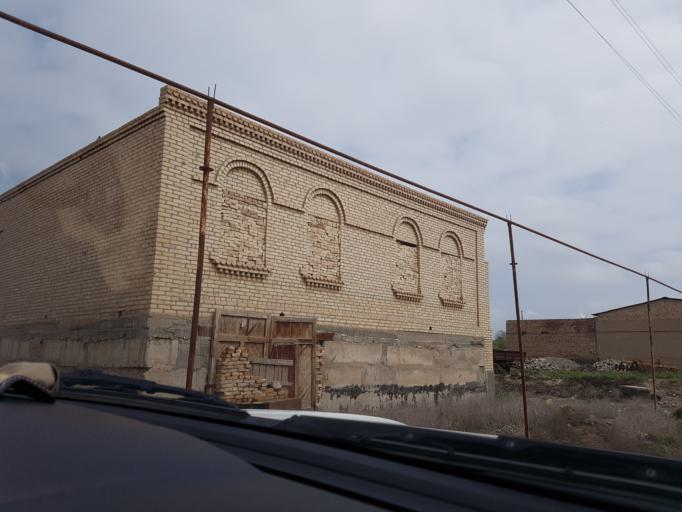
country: TM
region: Lebap
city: Turkmenabat
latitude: 38.9711
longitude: 63.6928
